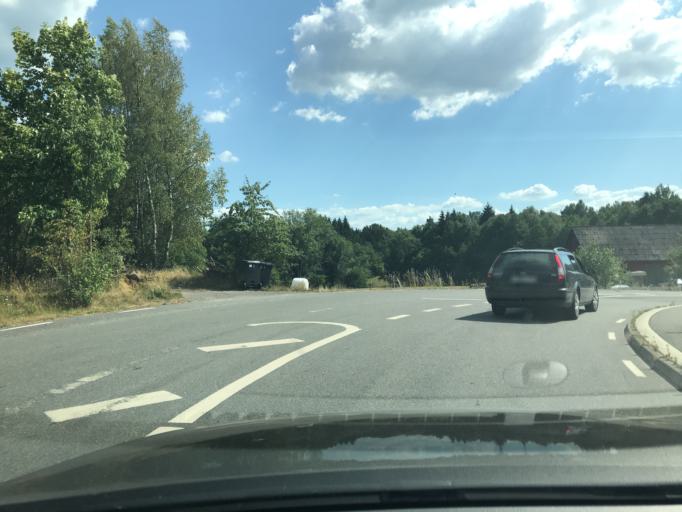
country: SE
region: Skane
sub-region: Hassleholms Kommun
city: Hastveda
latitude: 56.2747
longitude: 13.9131
